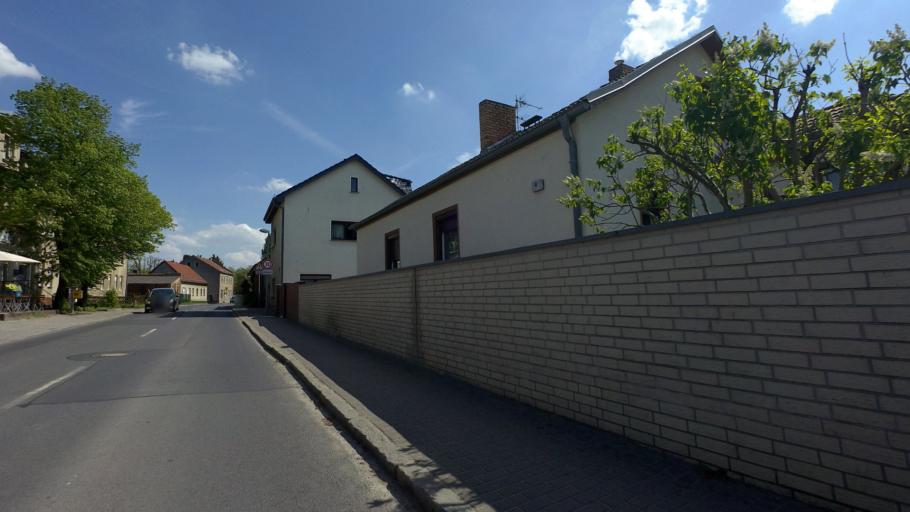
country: DE
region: Berlin
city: Blankenfelde
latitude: 52.6653
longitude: 13.3797
